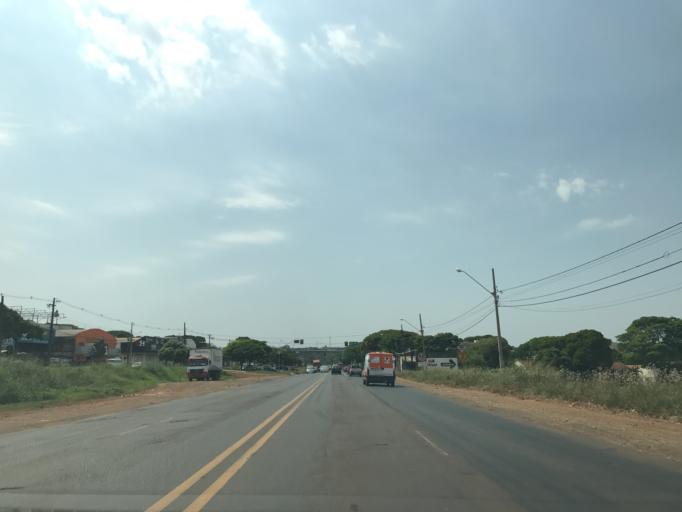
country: BR
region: Parana
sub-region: Sarandi
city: Sarandi
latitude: -23.4423
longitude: -51.8962
